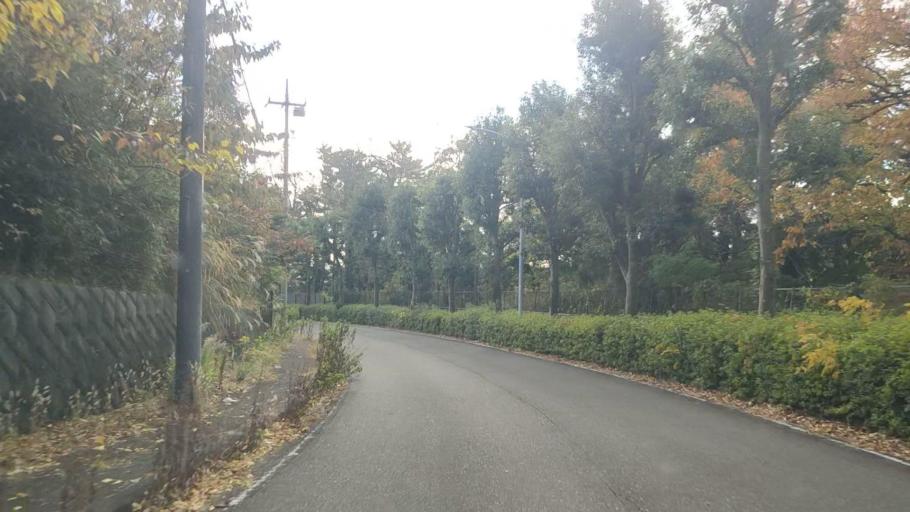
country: JP
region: Kanagawa
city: Yokohama
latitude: 35.4496
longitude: 139.5450
